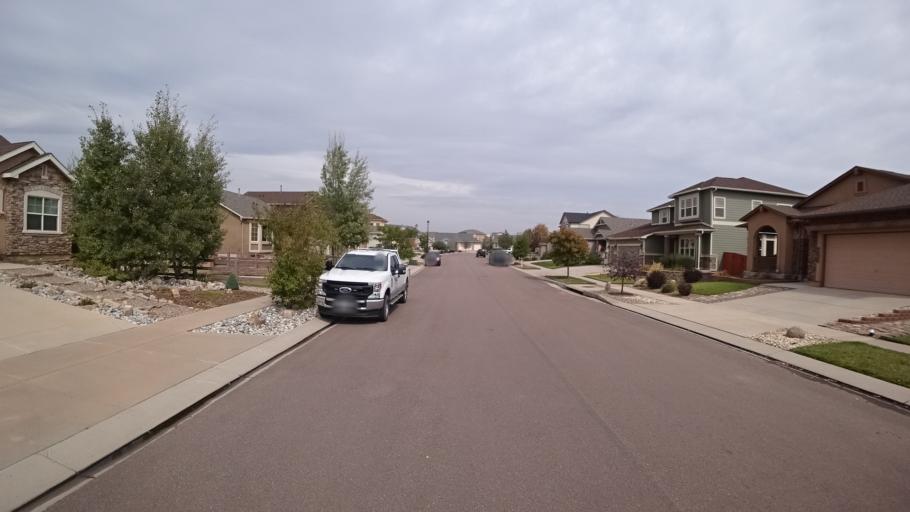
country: US
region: Colorado
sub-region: El Paso County
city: Cimarron Hills
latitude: 38.9224
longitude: -104.6914
